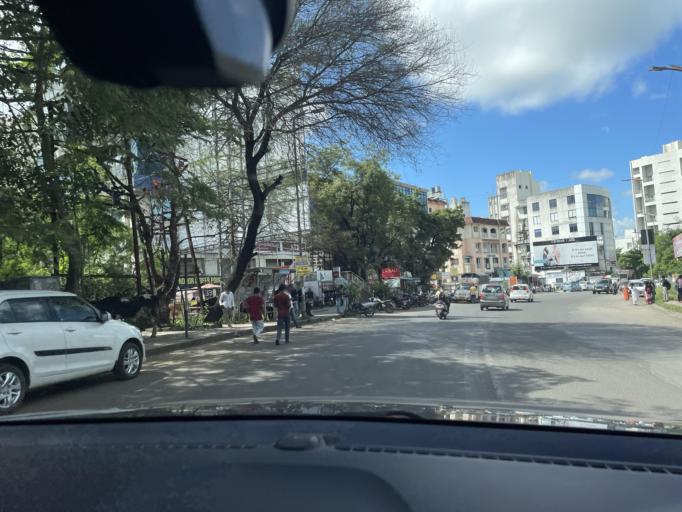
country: IN
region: Maharashtra
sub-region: Pune Division
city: Shivaji Nagar
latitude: 18.5188
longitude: 73.7790
